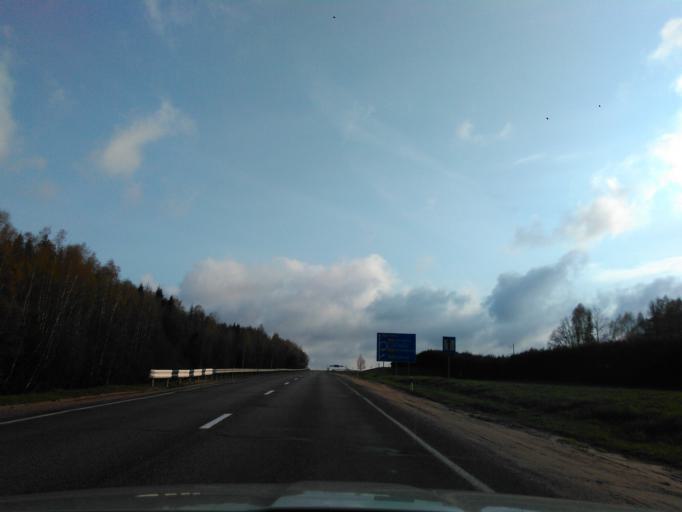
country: BY
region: Minsk
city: Lahoysk
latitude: 54.2147
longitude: 27.8287
